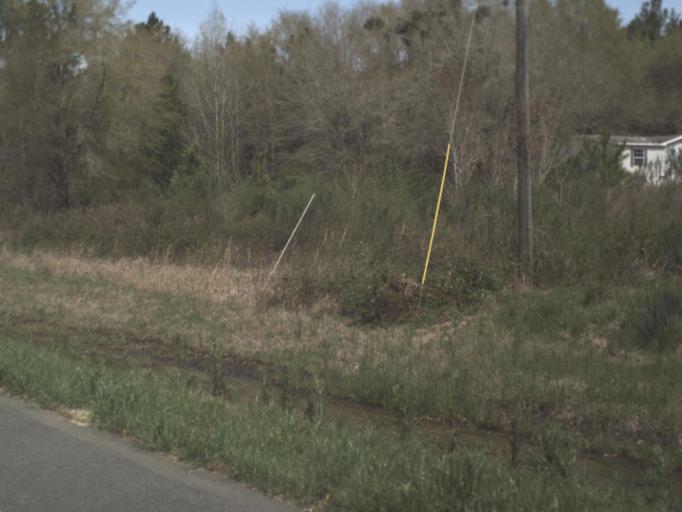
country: US
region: Alabama
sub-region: Geneva County
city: Geneva
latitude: 30.9672
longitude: -85.9979
